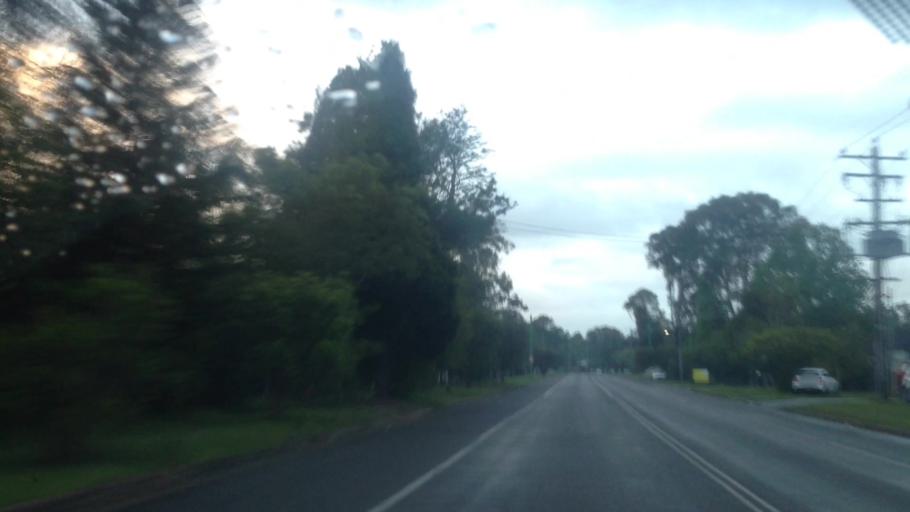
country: AU
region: New South Wales
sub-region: Lake Macquarie Shire
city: Cooranbong
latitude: -33.0823
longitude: 151.4473
